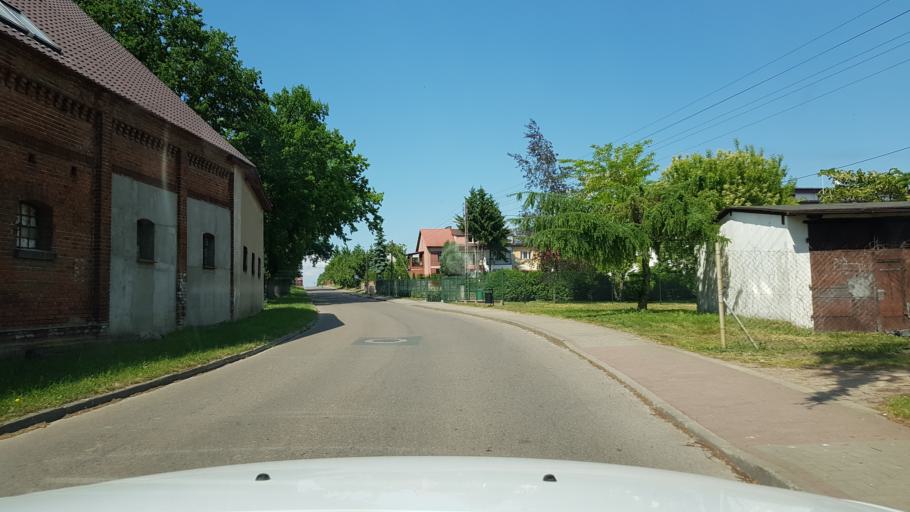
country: PL
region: West Pomeranian Voivodeship
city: Trzcinsko Zdroj
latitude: 52.9707
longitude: 14.6058
